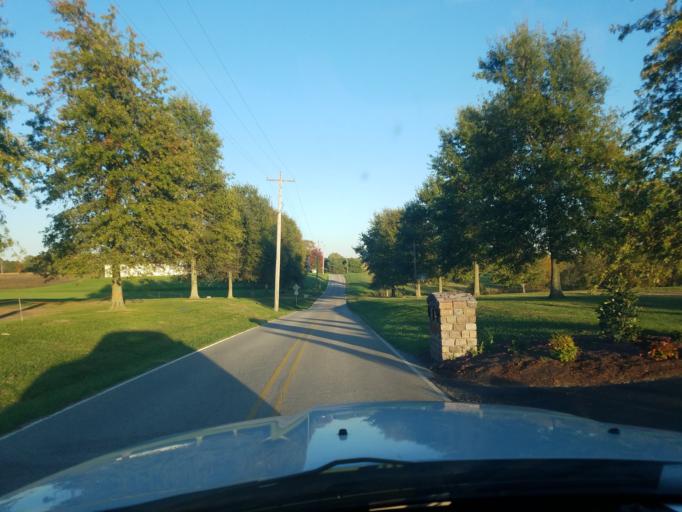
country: US
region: Indiana
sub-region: Floyd County
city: Galena
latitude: 38.4150
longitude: -85.9149
